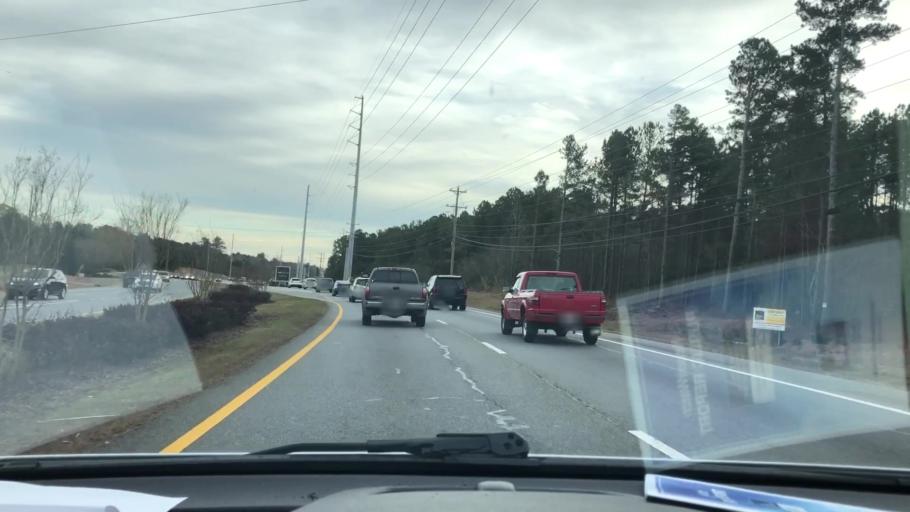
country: US
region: Georgia
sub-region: Forsyth County
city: Cumming
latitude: 34.1341
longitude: -84.1739
